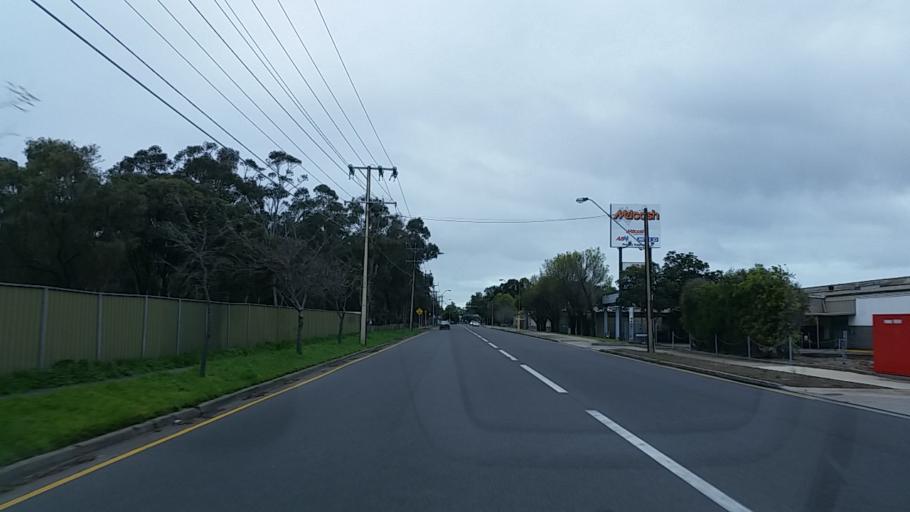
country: AU
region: South Australia
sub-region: Charles Sturt
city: Findon
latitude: -34.9156
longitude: 138.5346
